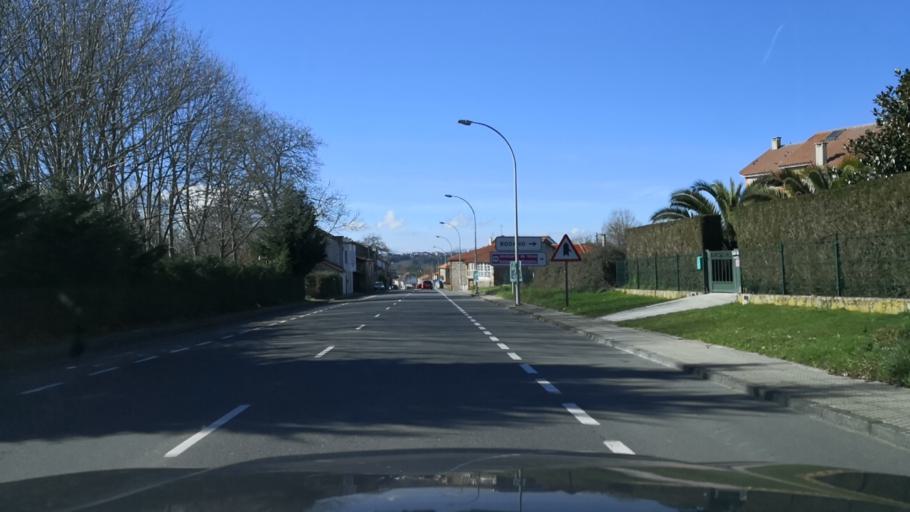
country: ES
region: Galicia
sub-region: Provincia de Pontevedra
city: Silleda
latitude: 42.6827
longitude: -8.1822
